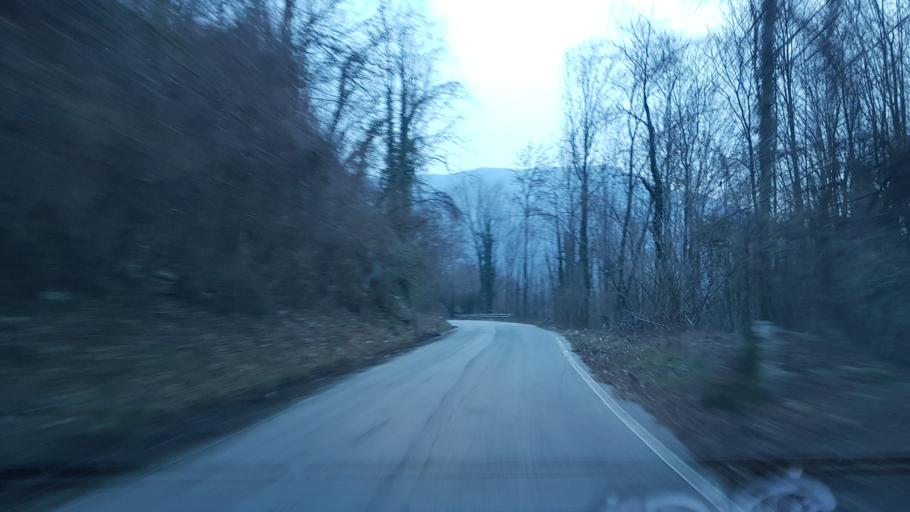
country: IT
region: Friuli Venezia Giulia
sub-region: Provincia di Udine
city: Attimis
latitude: 46.2012
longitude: 13.3404
